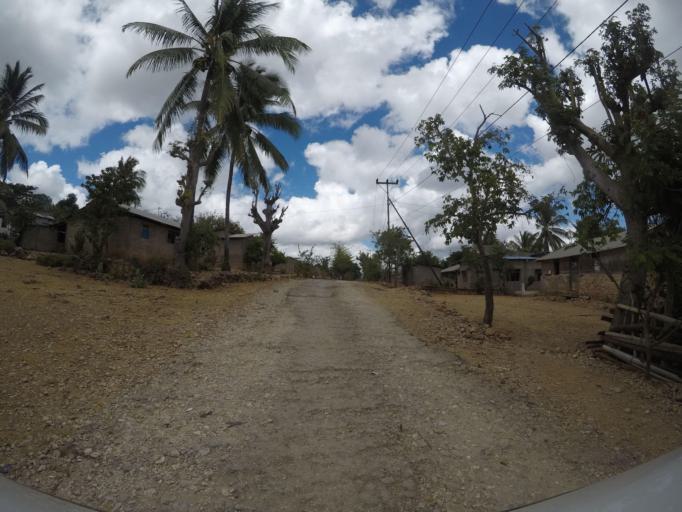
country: TL
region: Lautem
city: Lospalos
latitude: -8.3824
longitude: 126.9205
